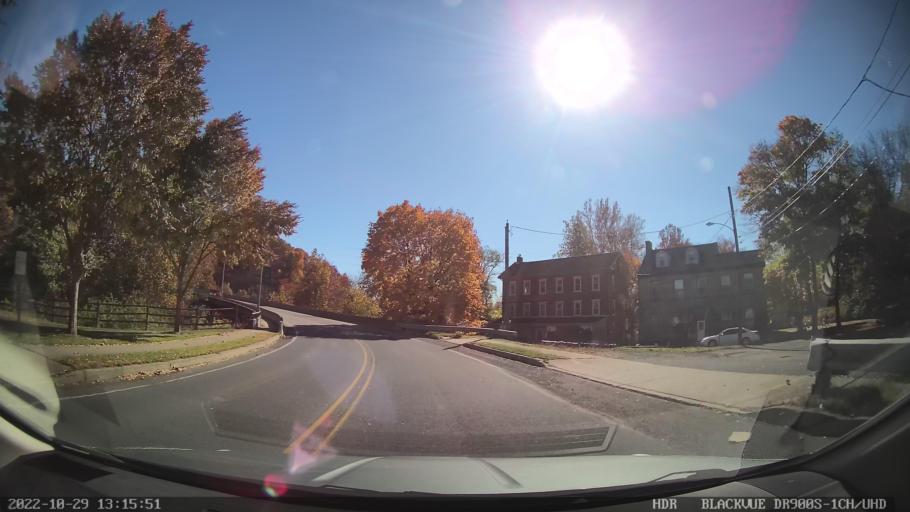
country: US
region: Pennsylvania
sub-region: Northampton County
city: Freemansburg
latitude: 40.6229
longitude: -75.3352
